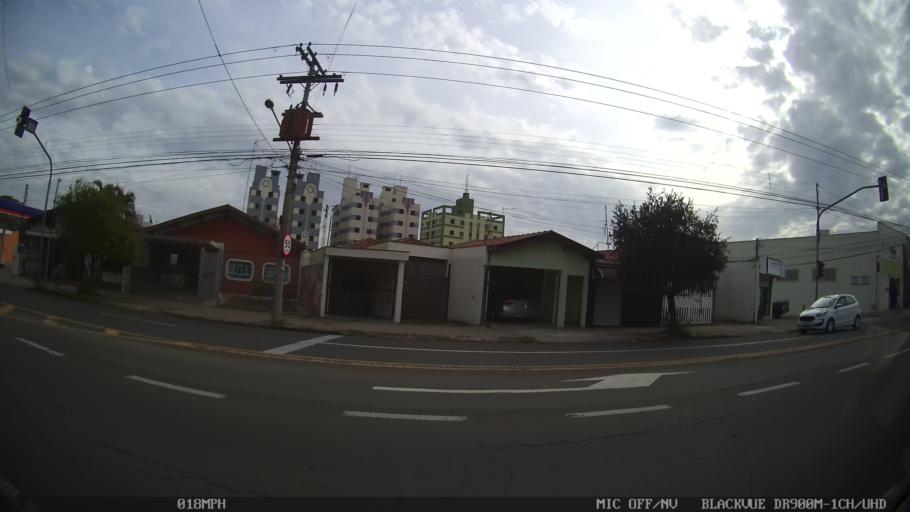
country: BR
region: Sao Paulo
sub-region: Piracicaba
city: Piracicaba
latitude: -22.7410
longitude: -47.6413
